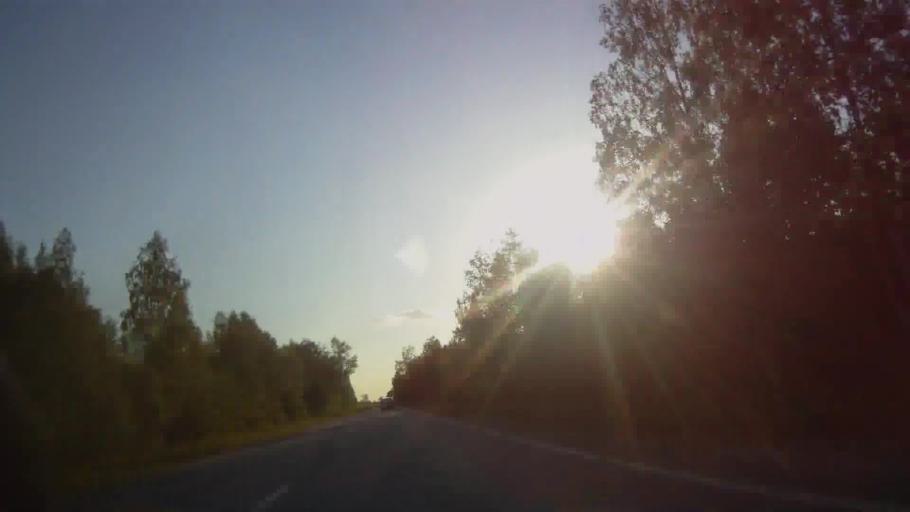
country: LV
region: Livani
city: Livani
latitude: 56.5306
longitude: 26.3556
